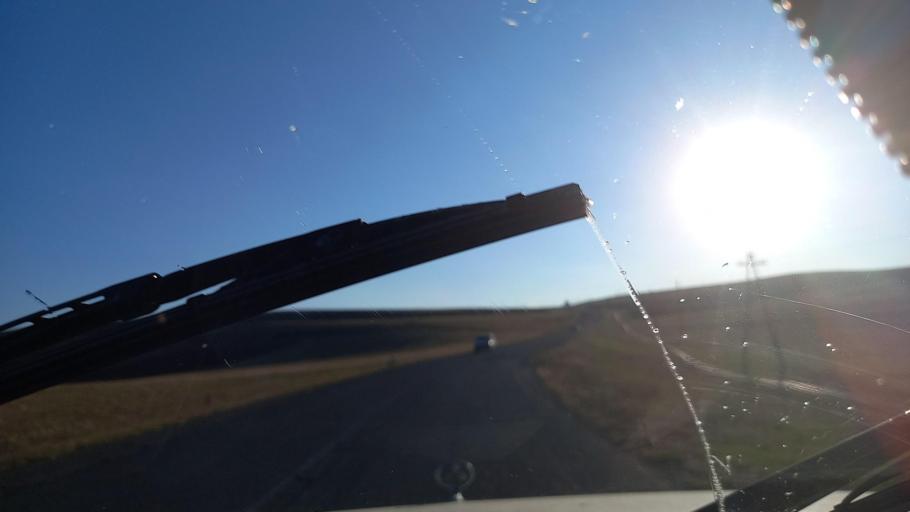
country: AZ
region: Shamkir Rayon
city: Shamkhor
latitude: 40.7610
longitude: 45.9173
